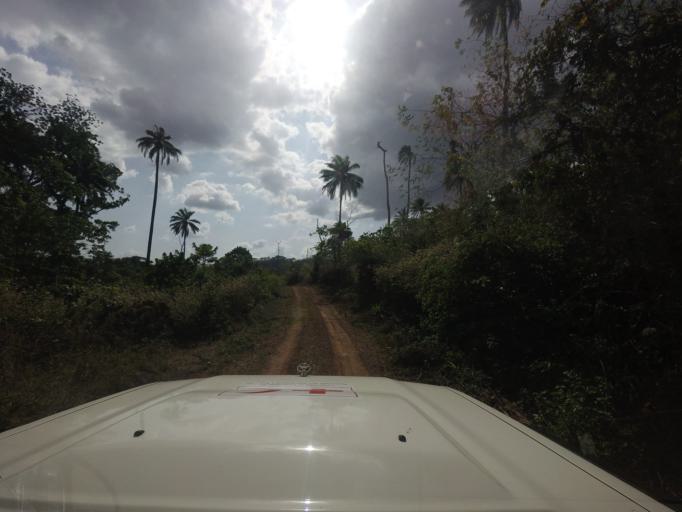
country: LR
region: Lofa
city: Voinjama
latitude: 8.3930
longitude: -9.6170
